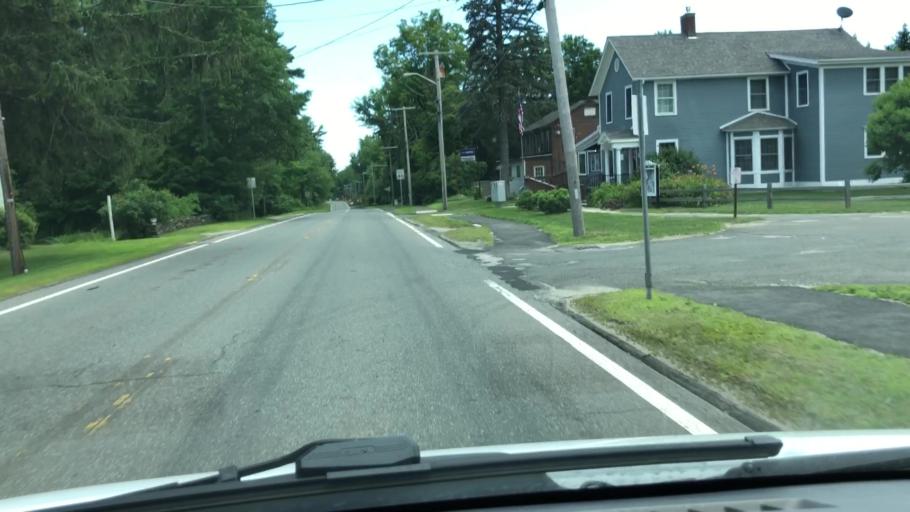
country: US
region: Massachusetts
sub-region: Hampshire County
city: Chesterfield
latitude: 42.4405
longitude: -72.7998
